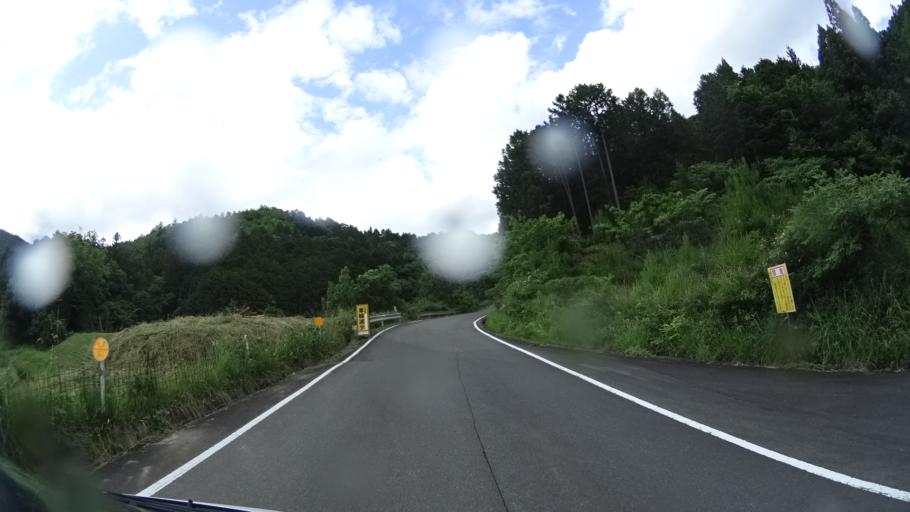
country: JP
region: Kyoto
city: Ayabe
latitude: 35.3507
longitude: 135.1979
